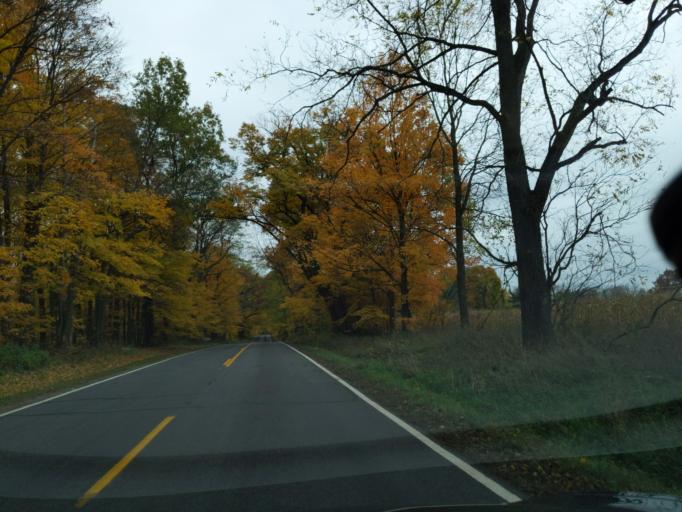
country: US
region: Michigan
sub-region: Jackson County
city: Spring Arbor
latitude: 42.3412
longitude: -84.6005
